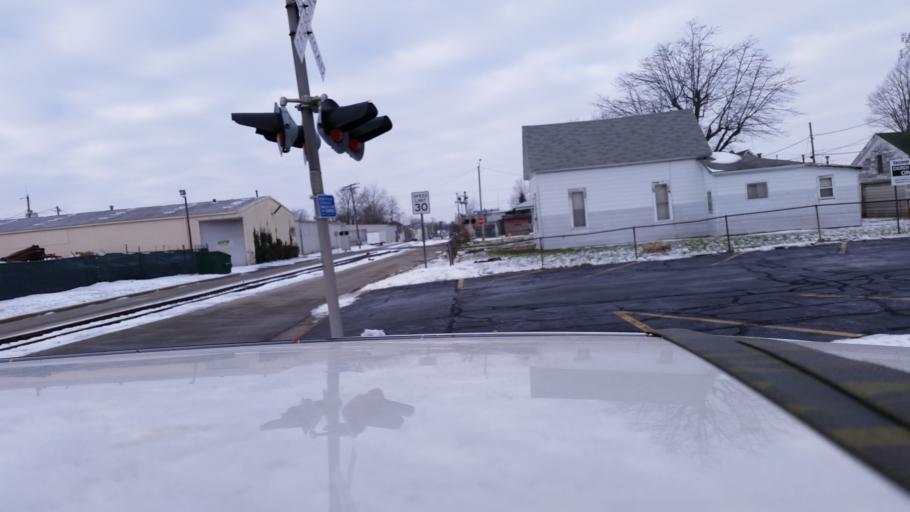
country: US
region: Indiana
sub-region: Howard County
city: Kokomo
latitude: 40.4929
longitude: -86.1269
